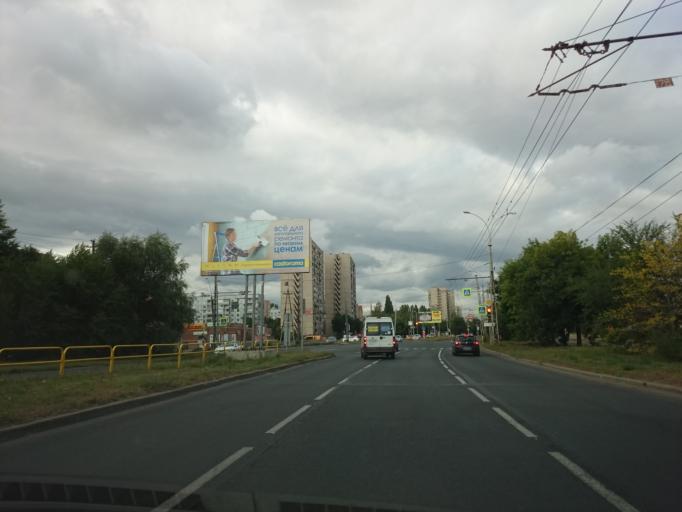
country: RU
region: Samara
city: Tol'yatti
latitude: 53.5038
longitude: 49.2997
